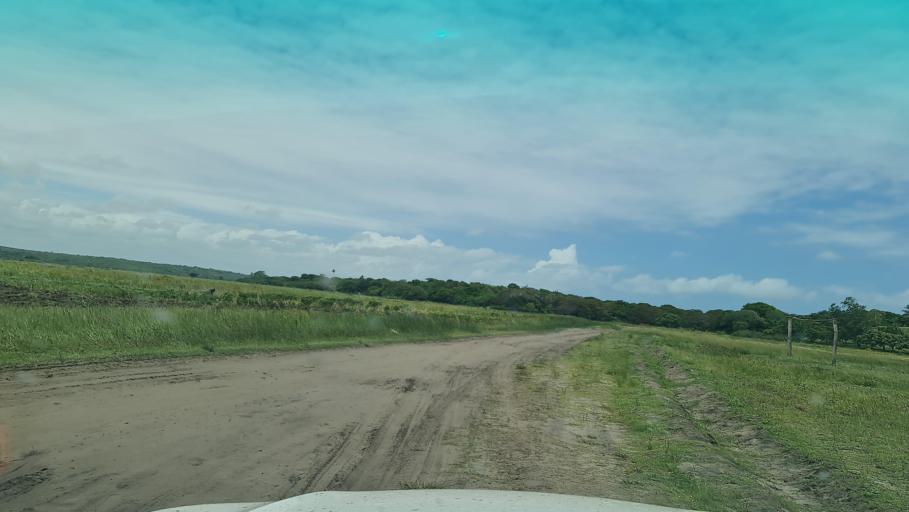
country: MZ
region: Maputo
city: Manhica
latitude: -25.5245
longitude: 32.8573
